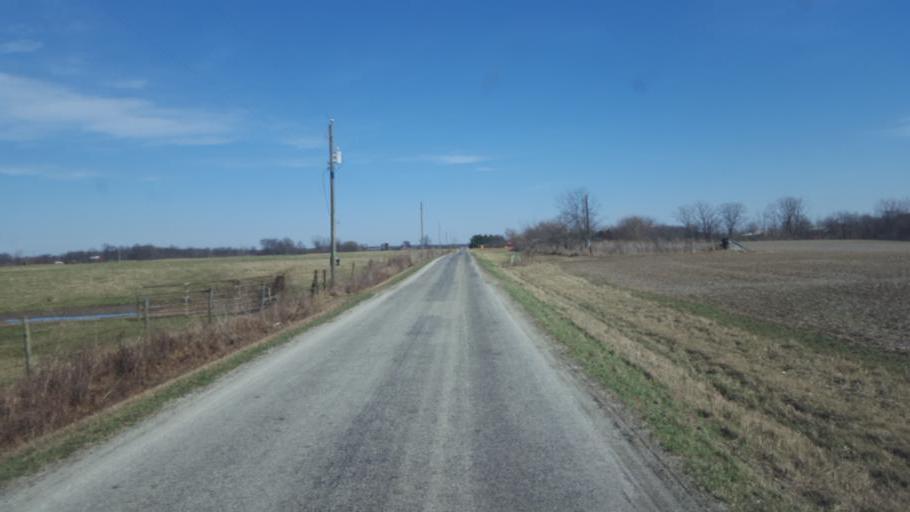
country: US
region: Ohio
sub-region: Union County
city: Richwood
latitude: 40.5594
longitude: -83.3983
